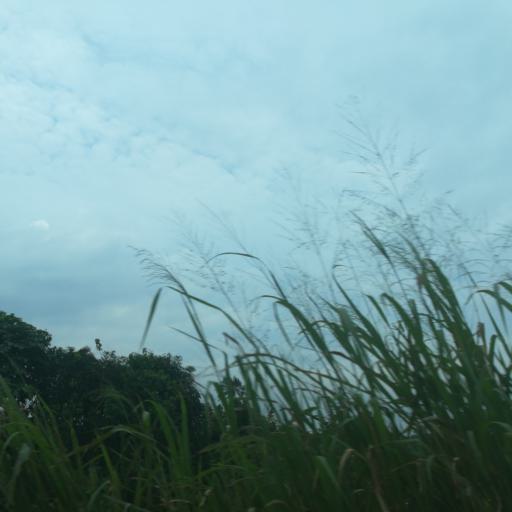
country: NG
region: Lagos
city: Ejirin
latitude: 6.6468
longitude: 3.7591
